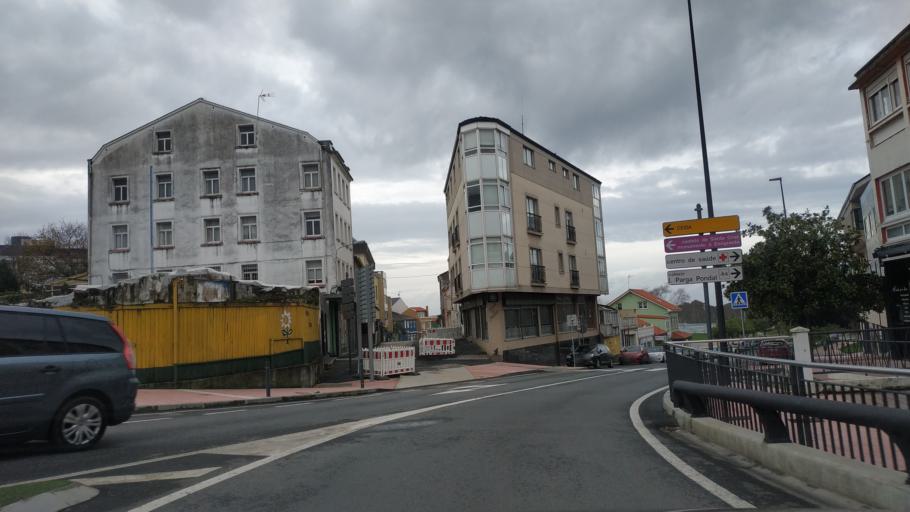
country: ES
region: Galicia
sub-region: Provincia da Coruna
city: Oleiros
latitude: 43.3466
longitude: -8.3455
